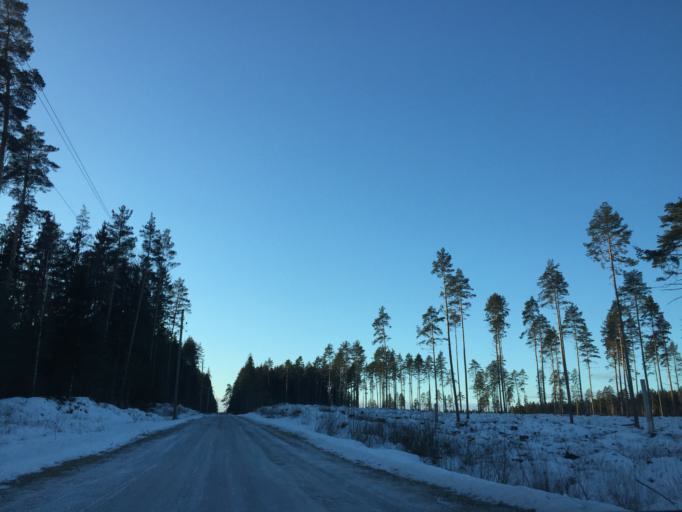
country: LV
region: Kegums
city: Kegums
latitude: 56.7373
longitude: 24.6648
